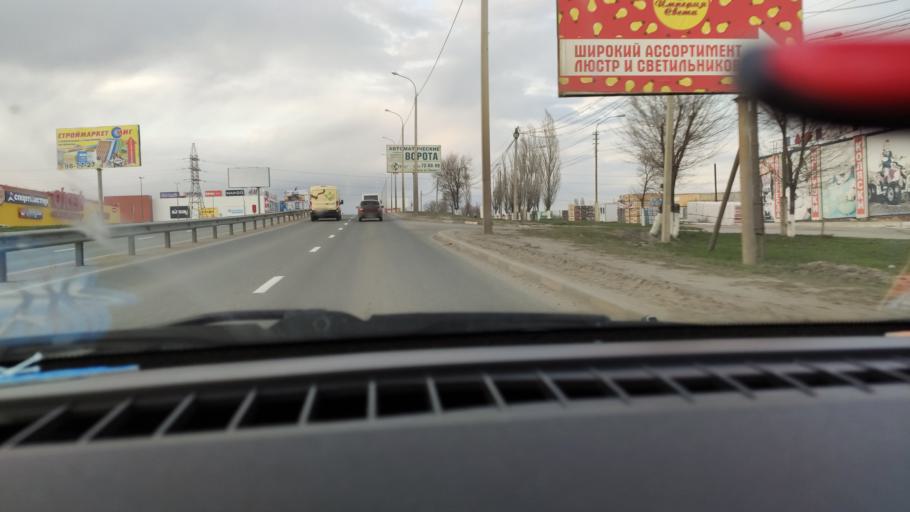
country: RU
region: Saratov
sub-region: Saratovskiy Rayon
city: Saratov
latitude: 51.6229
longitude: 45.9762
